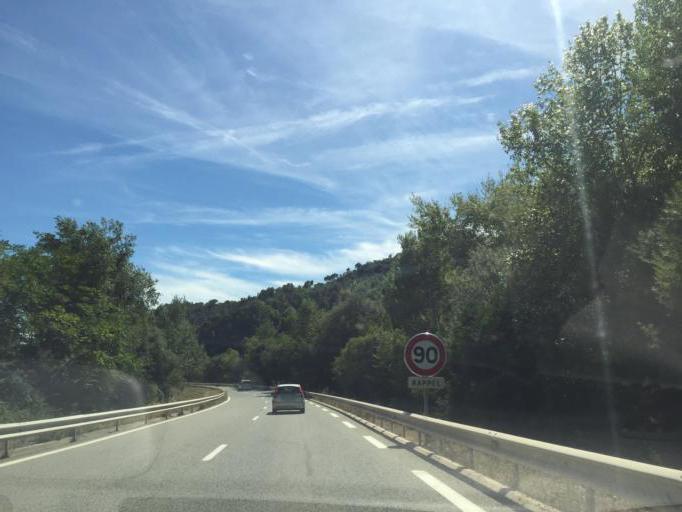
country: FR
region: Provence-Alpes-Cote d'Azur
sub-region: Departement des Alpes-Maritimes
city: Levens
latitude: 43.8588
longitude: 7.1968
